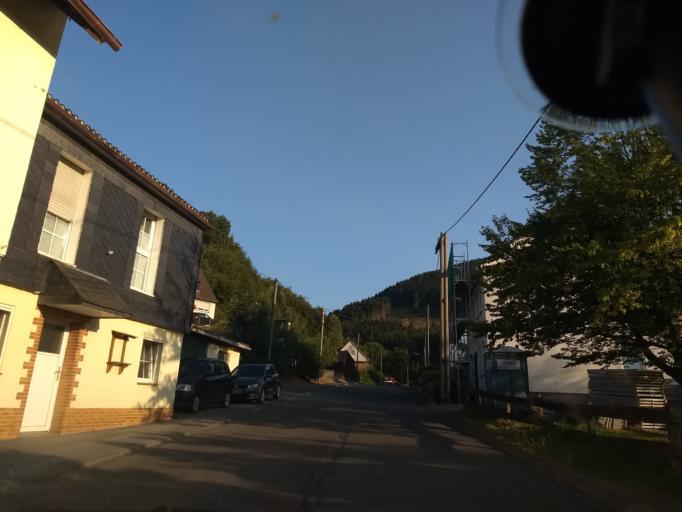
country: DE
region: North Rhine-Westphalia
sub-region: Regierungsbezirk Arnsberg
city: Sundern
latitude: 51.3091
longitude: 8.0727
